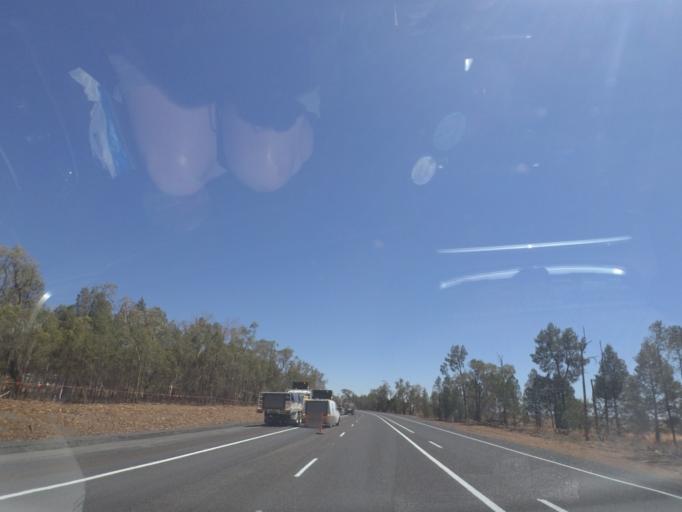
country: AU
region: New South Wales
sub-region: Gilgandra
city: Gilgandra
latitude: -31.6639
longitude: 148.7199
